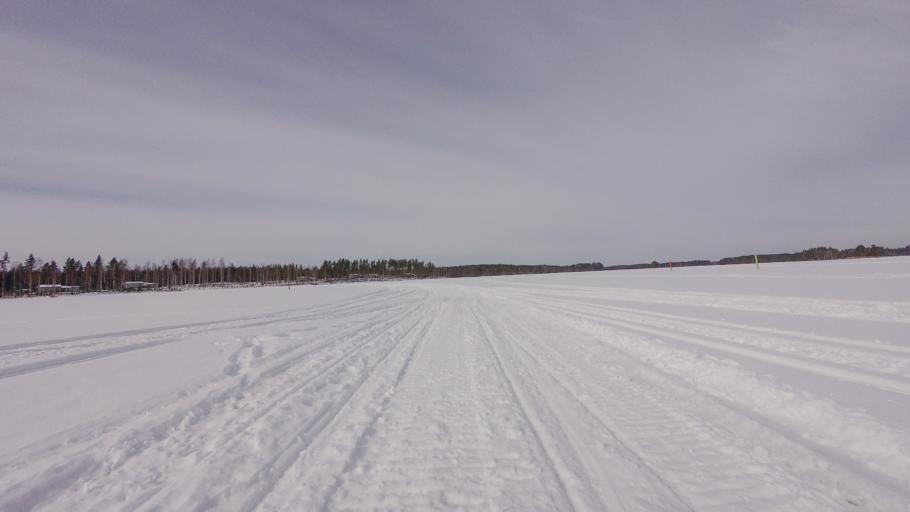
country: FI
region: Southern Savonia
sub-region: Savonlinna
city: Heinaevesi
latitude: 62.1251
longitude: 28.6038
